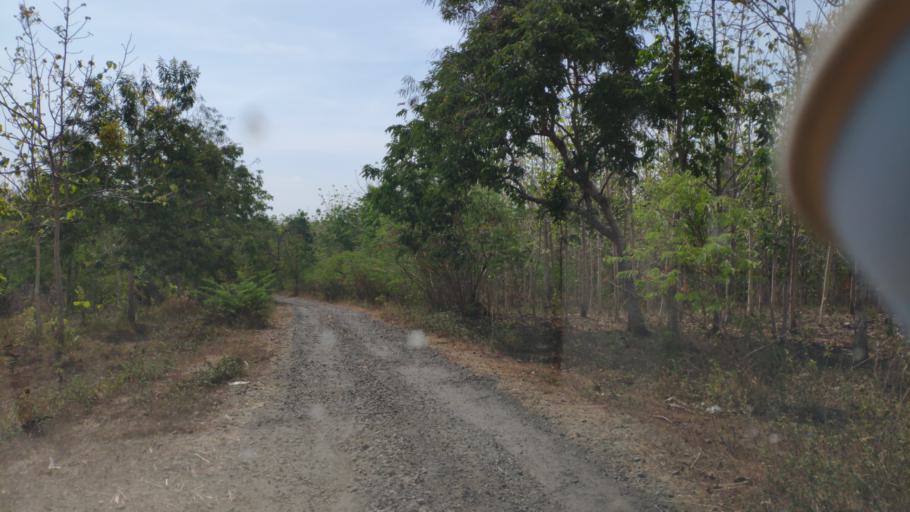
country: ID
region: Central Java
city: Balong Wetan
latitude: -7.0002
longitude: 111.2786
